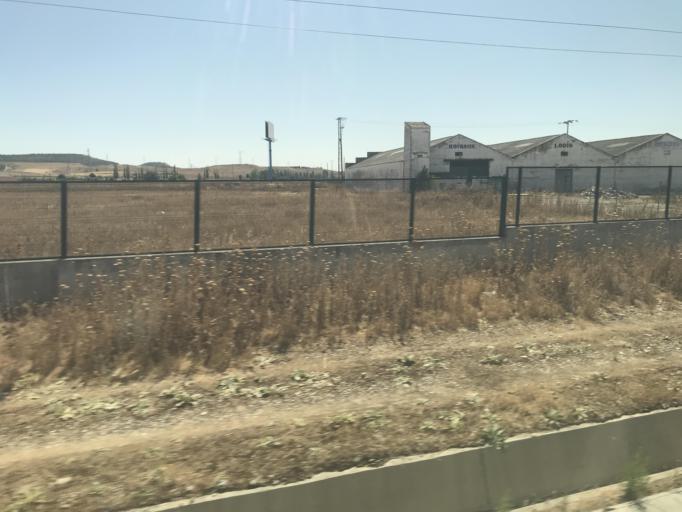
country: ES
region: Castille and Leon
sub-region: Provincia de Valladolid
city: Santovenia de Pisuerga
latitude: 41.6866
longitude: -4.6861
